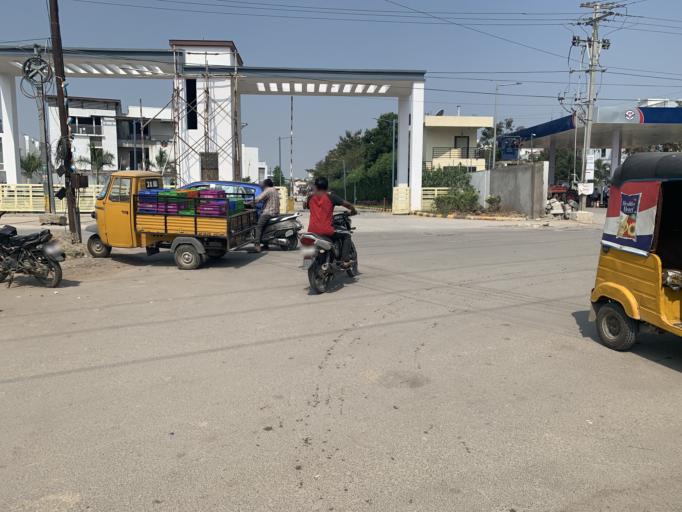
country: IN
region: Telangana
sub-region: Rangareddi
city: Kukatpalli
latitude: 17.4937
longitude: 78.4203
